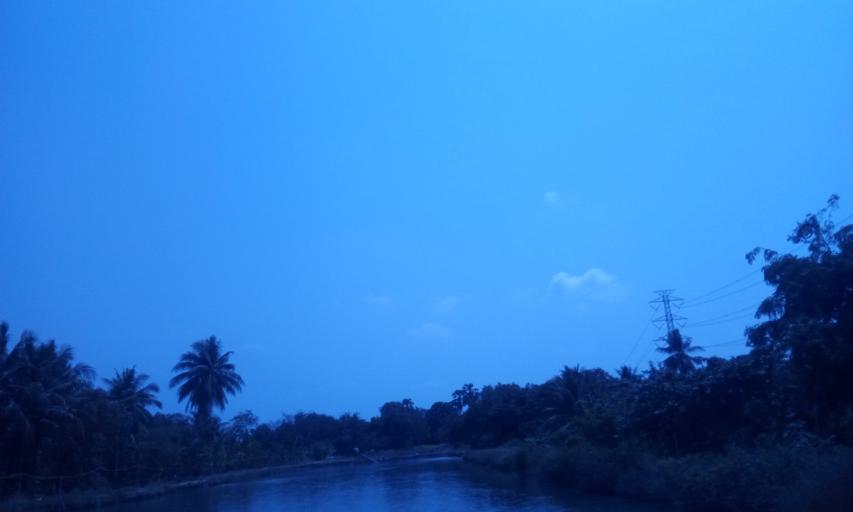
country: TH
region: Chachoengsao
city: Bang Nam Priao
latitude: 13.9069
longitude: 100.9732
